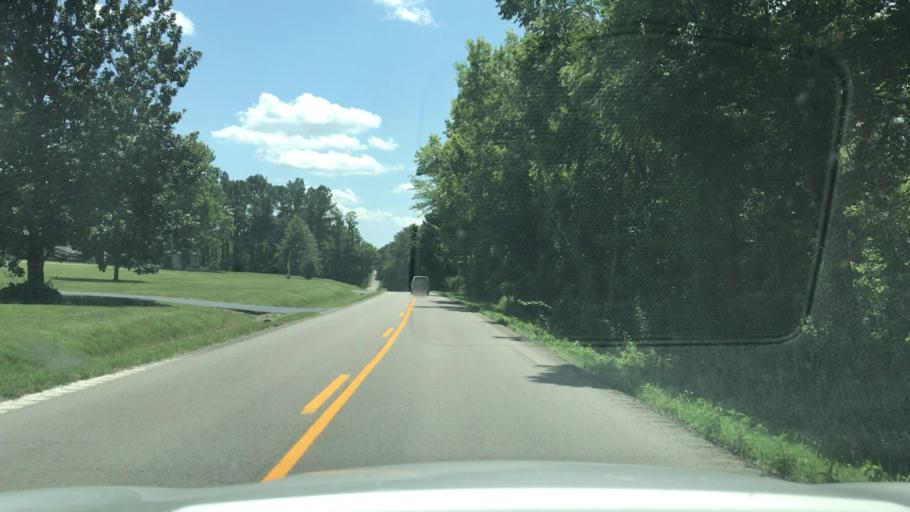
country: US
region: Kentucky
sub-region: Christian County
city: Hopkinsville
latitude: 36.9126
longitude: -87.4424
